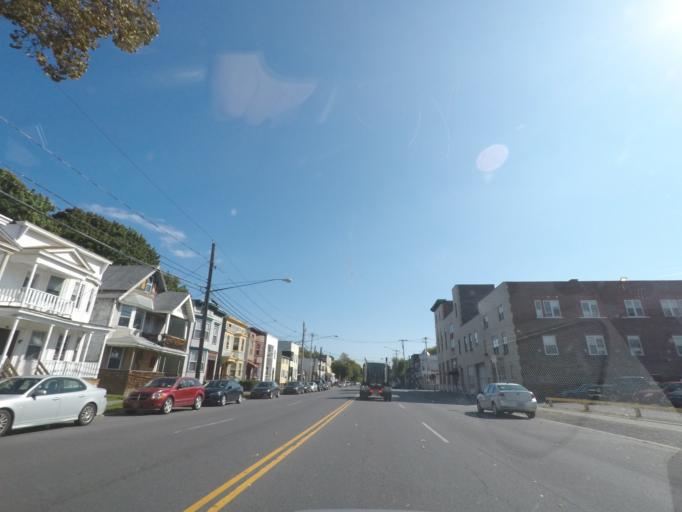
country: US
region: New York
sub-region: Albany County
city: West Albany
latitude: 42.6642
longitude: -73.7762
